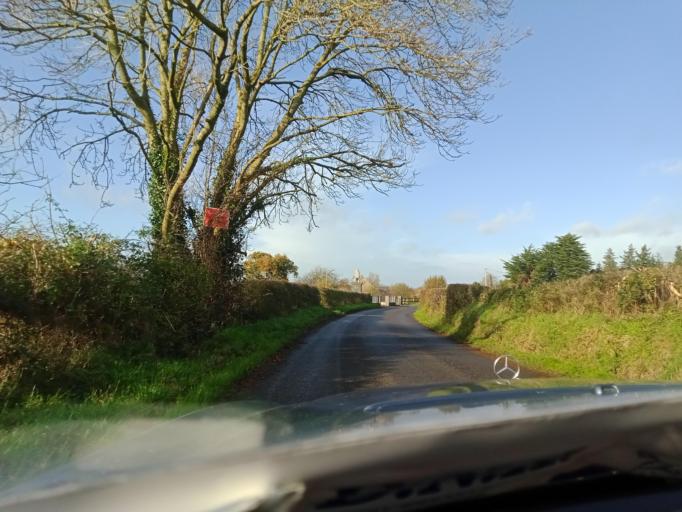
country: IE
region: Leinster
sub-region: Kilkenny
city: Mooncoin
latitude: 52.3325
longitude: -7.2589
